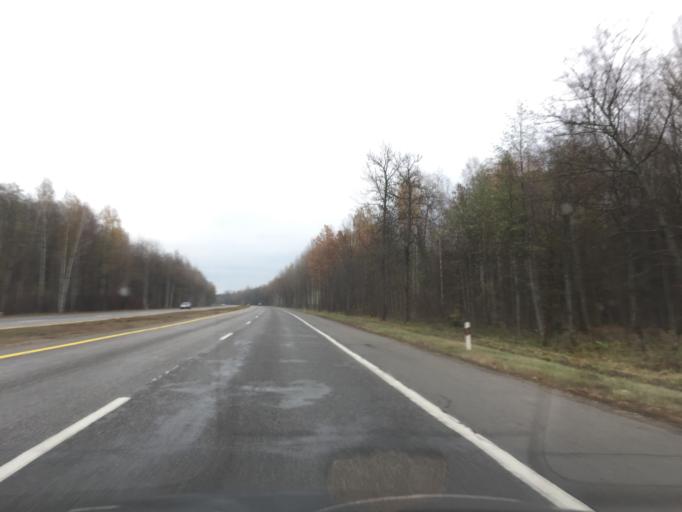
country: BY
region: Gomel
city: Horad Rechytsa
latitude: 52.3570
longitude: 30.6869
